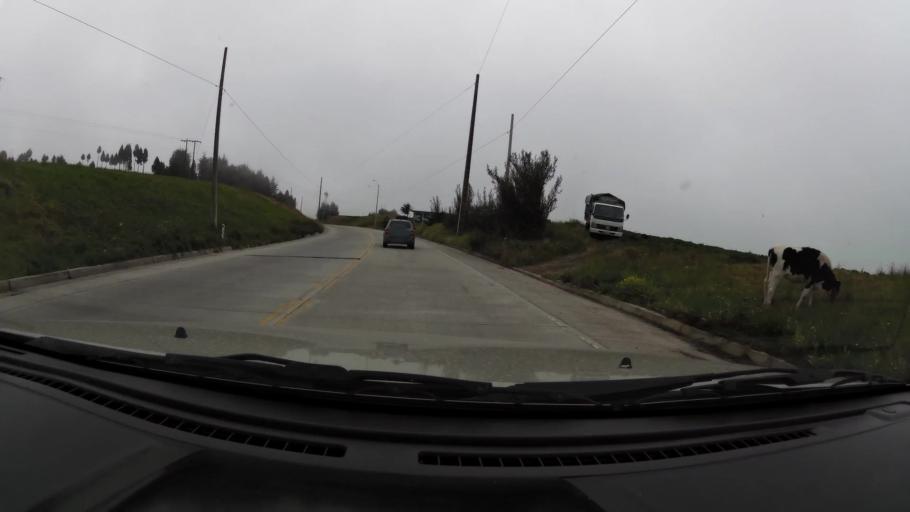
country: EC
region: Canar
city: Canar
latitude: -2.5856
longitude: -78.9190
